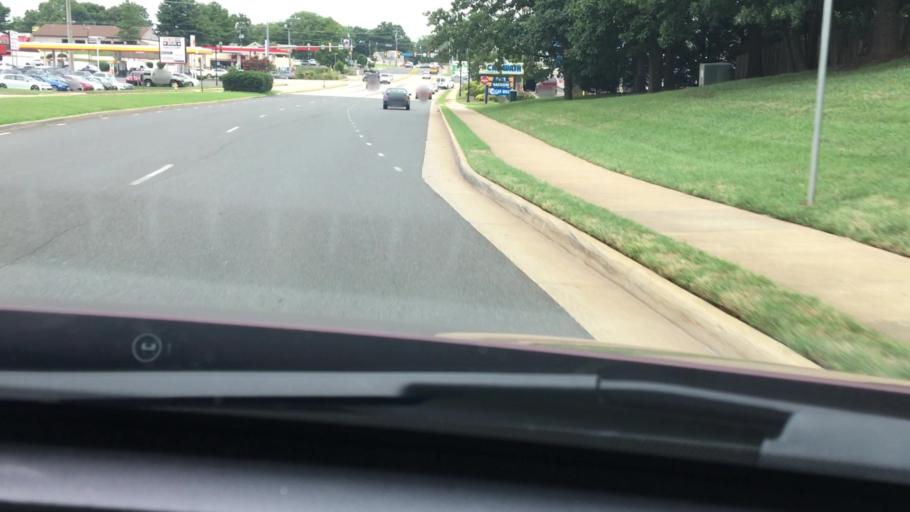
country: US
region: Virginia
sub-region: Prince William County
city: Yorkshire
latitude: 38.7715
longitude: -77.4506
